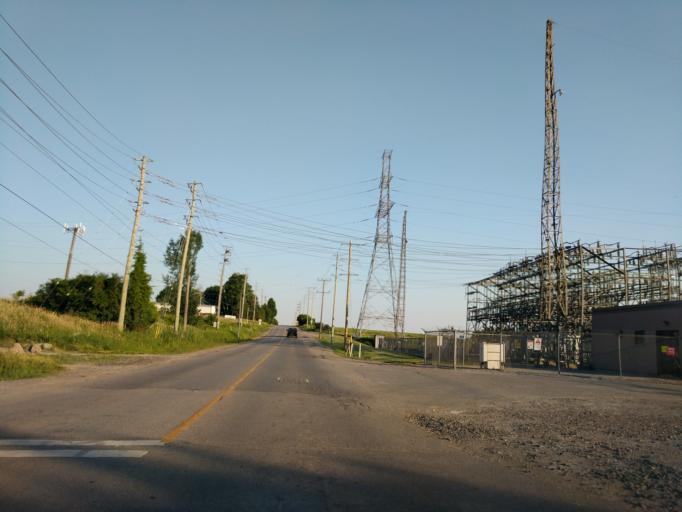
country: CA
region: Ontario
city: Oshawa
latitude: 43.8820
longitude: -78.8890
